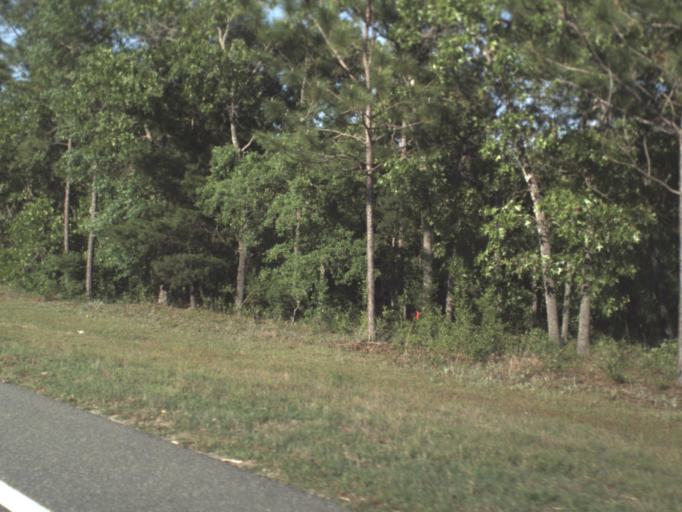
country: US
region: Florida
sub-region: Liberty County
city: Bristol
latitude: 30.4294
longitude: -84.7731
